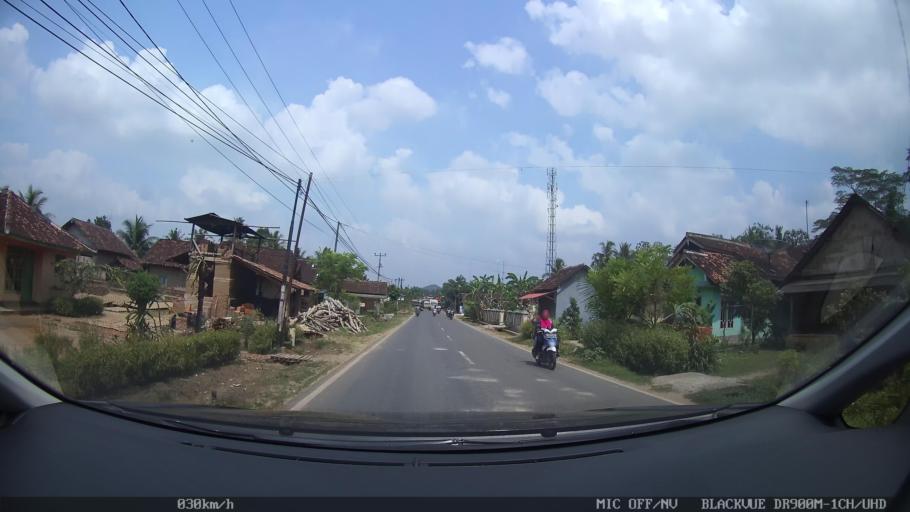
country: ID
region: Lampung
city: Pringsewu
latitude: -5.3874
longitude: 104.9680
